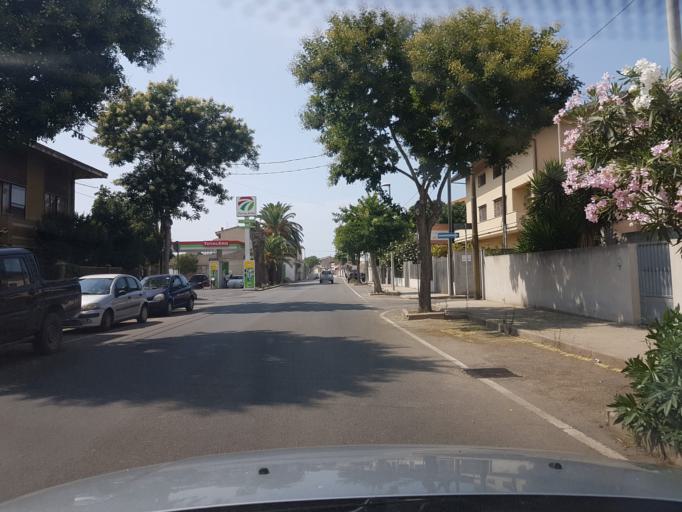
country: IT
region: Sardinia
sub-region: Provincia di Oristano
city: Cabras
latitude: 39.9241
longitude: 8.5392
